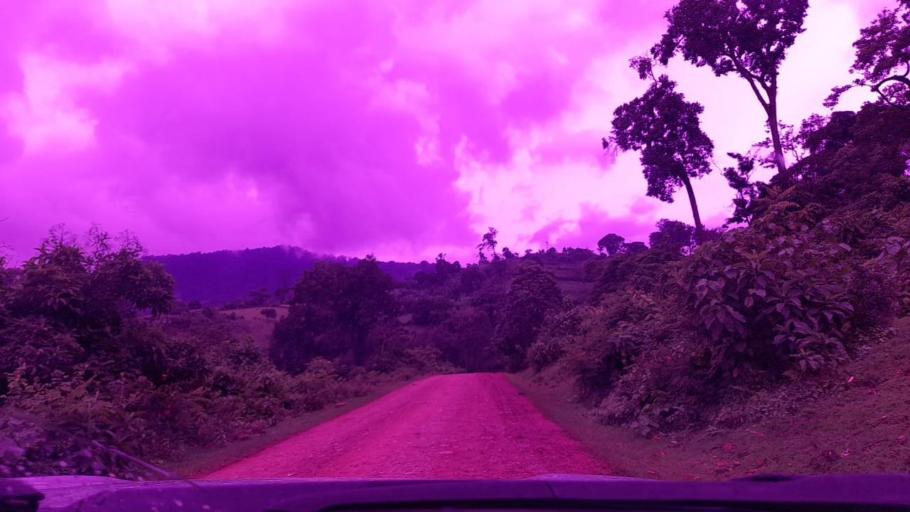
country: ET
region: Southern Nations, Nationalities, and People's Region
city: Bonga
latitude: 7.5616
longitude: 35.8386
